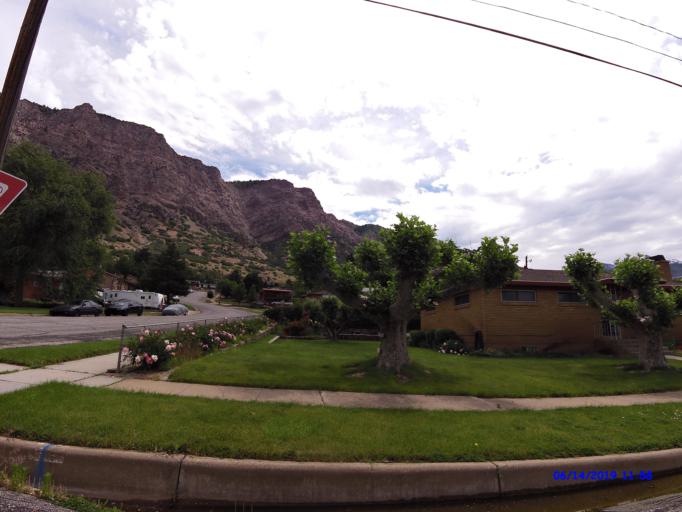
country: US
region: Utah
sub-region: Weber County
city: Ogden
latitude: 41.2600
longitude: -111.9448
